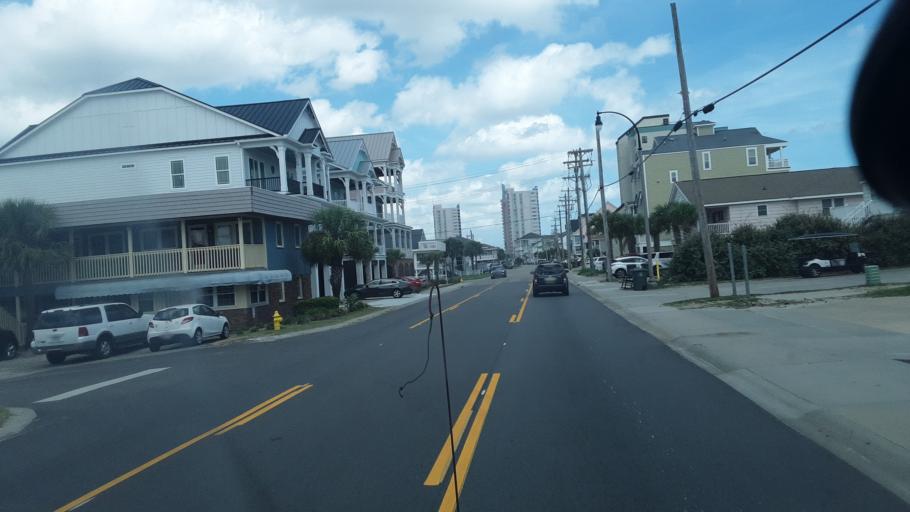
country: US
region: South Carolina
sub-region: Horry County
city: North Myrtle Beach
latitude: 33.8289
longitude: -78.6393
